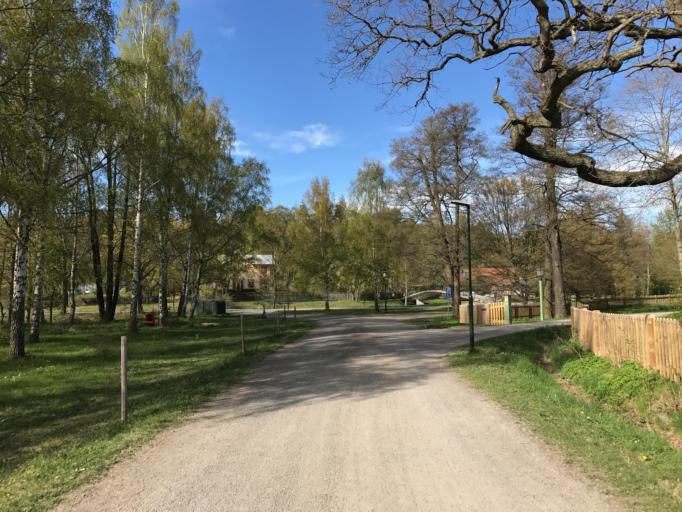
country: SE
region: Stockholm
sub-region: Nacka Kommun
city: Nacka
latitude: 59.3258
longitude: 18.1459
